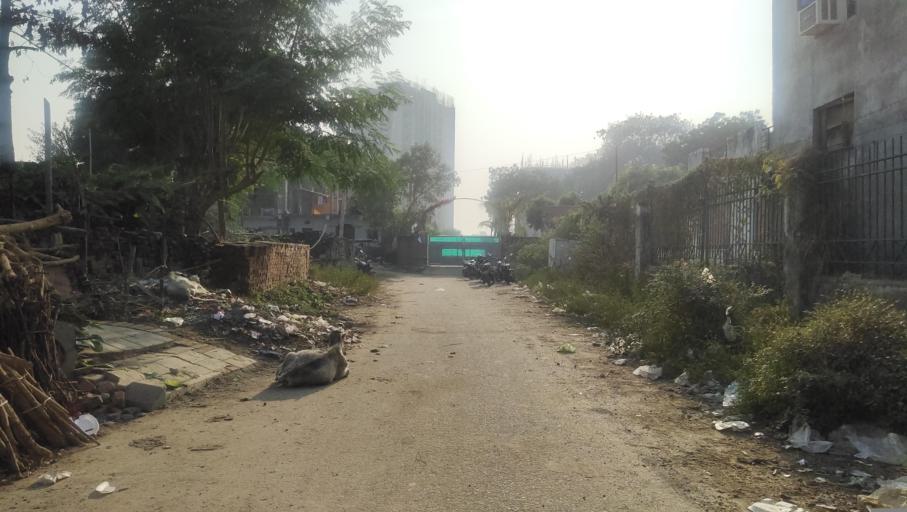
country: IN
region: Uttar Pradesh
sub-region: Lucknow District
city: Goshainganj
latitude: 26.7911
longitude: 81.0118
